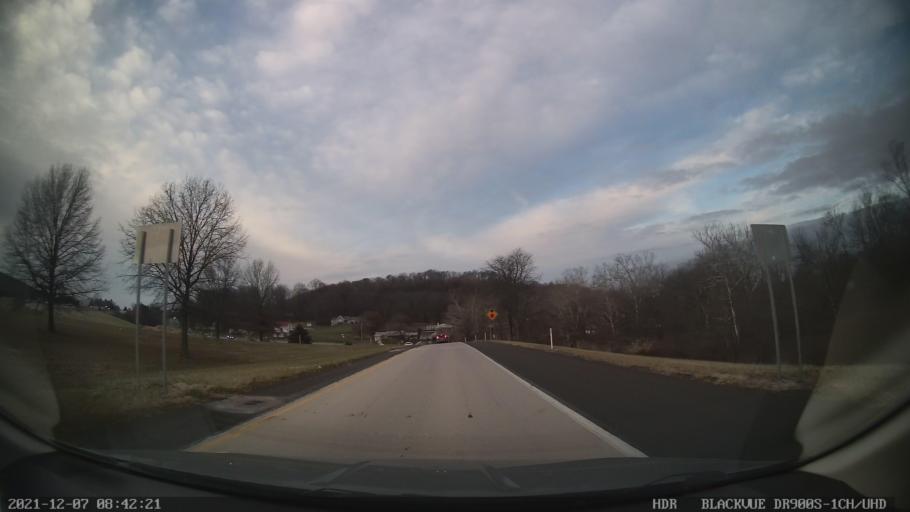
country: US
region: Pennsylvania
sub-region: Berks County
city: South Temple
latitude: 40.3786
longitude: -75.8985
